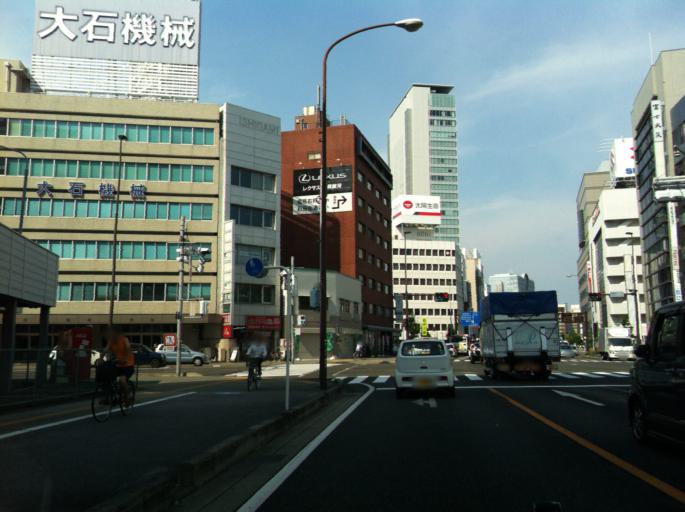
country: JP
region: Shizuoka
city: Shizuoka-shi
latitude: 34.9703
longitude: 138.3842
